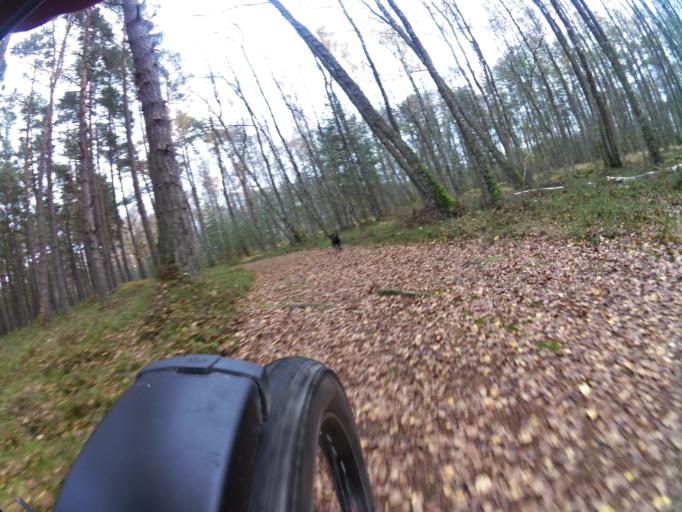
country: PL
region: Pomeranian Voivodeship
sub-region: Powiat leborski
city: Leba
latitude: 54.7669
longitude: 17.6011
